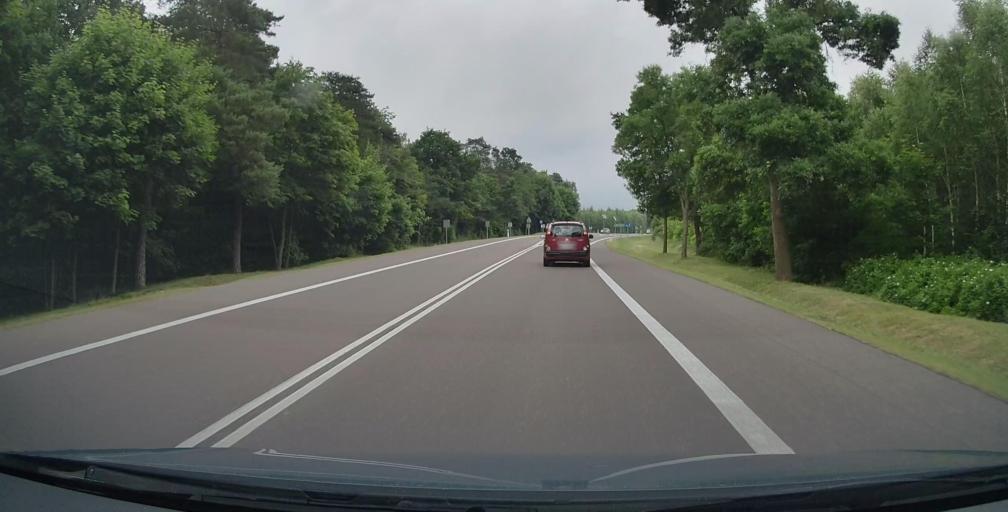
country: PL
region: Lublin Voivodeship
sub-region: Powiat bialski
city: Lesna Podlaska
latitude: 52.0384
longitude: 22.9440
